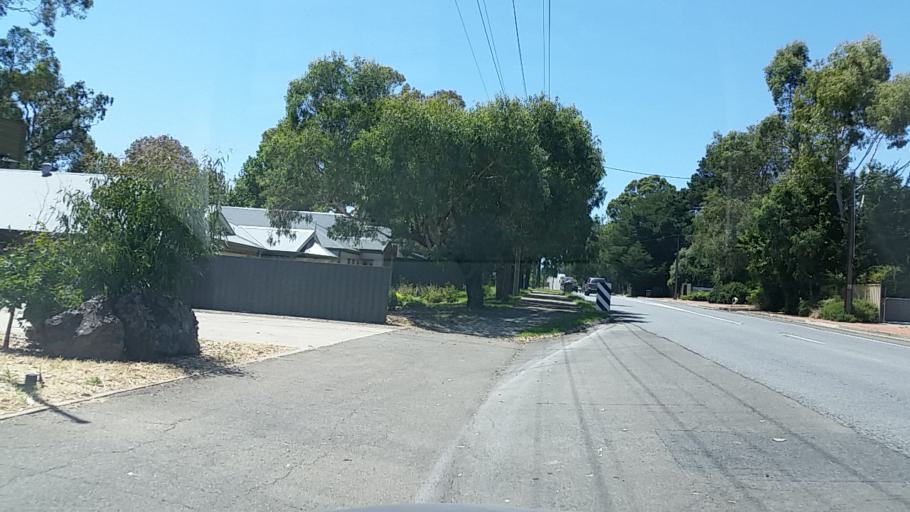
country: AU
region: South Australia
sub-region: Mount Barker
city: Mount Barker
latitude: -35.0471
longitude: 138.8697
